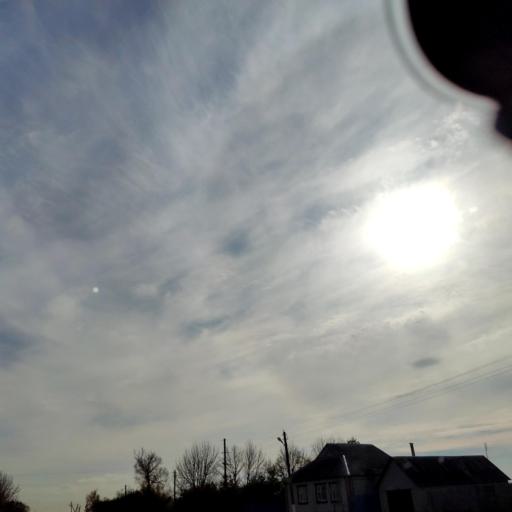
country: RU
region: Voronezj
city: Rossosh'
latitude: 51.1954
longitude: 38.7785
